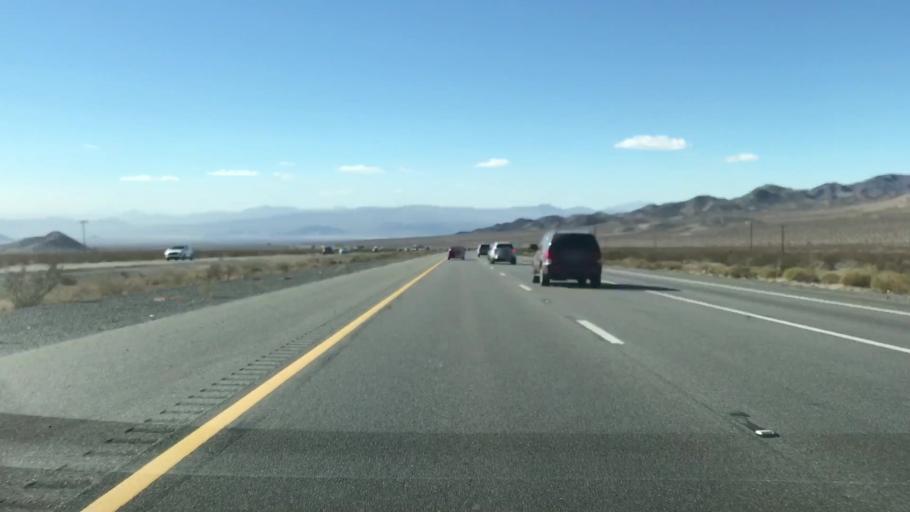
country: US
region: Nevada
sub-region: Clark County
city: Sandy Valley
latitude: 35.3726
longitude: -115.8977
